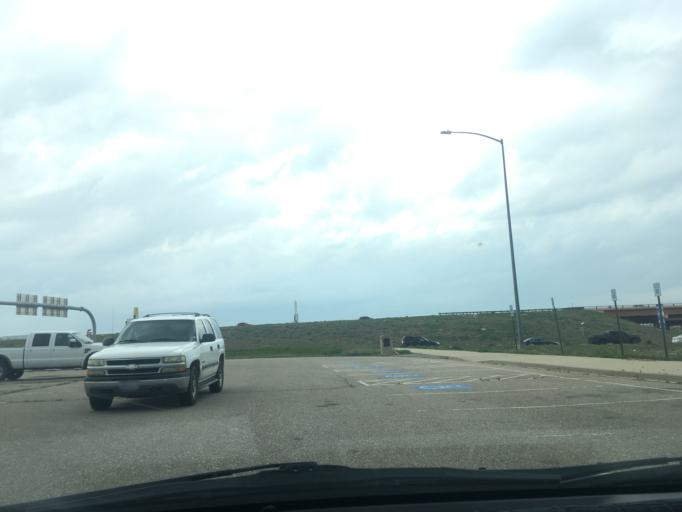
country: US
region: Colorado
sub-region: Weld County
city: Firestone
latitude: 40.1596
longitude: -104.9769
